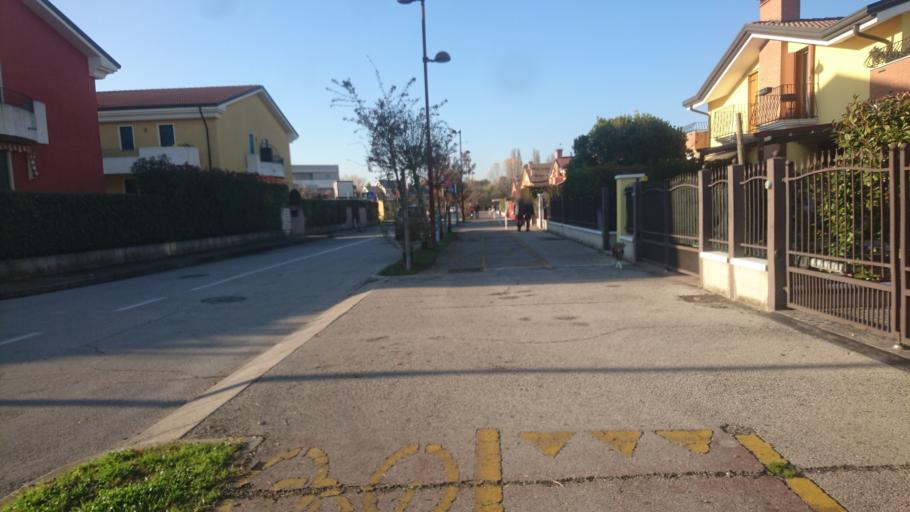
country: IT
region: Veneto
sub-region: Provincia di Padova
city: Villaguattera
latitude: 45.4466
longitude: 11.8169
